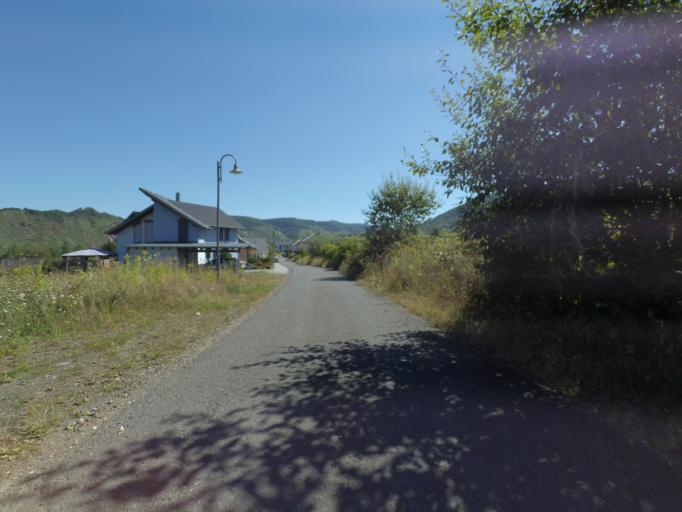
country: DE
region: Rheinland-Pfalz
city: Bremm
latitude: 50.0962
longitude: 7.1195
